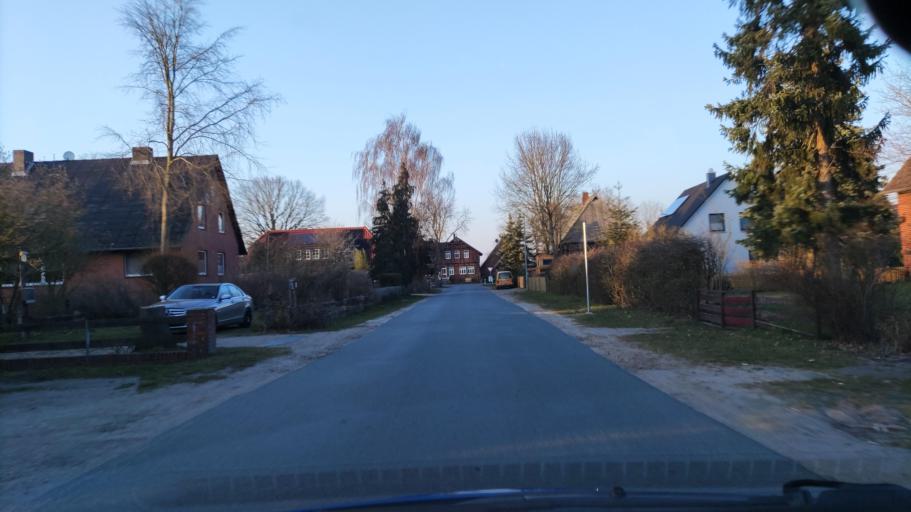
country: DE
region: Lower Saxony
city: Dannenberg
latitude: 53.1087
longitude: 11.1353
